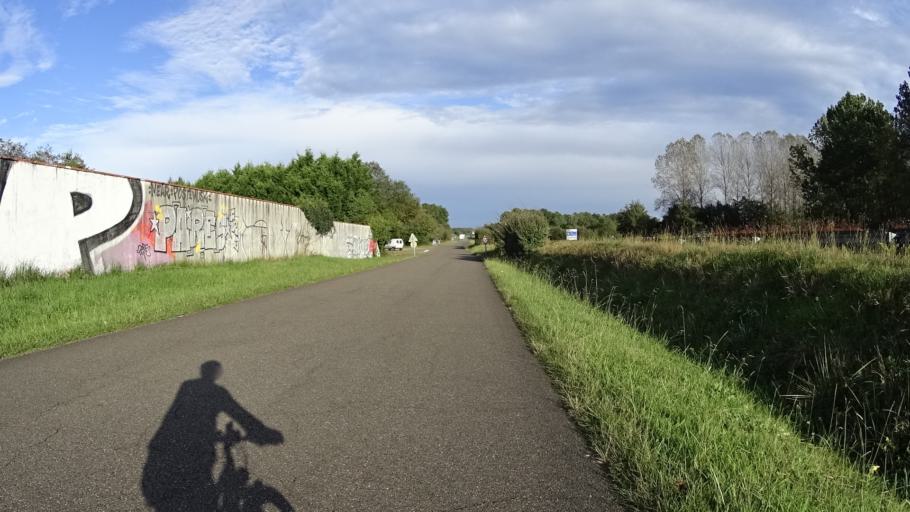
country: FR
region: Aquitaine
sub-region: Departement des Landes
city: Saint-Paul-les-Dax
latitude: 43.7421
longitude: -1.0711
